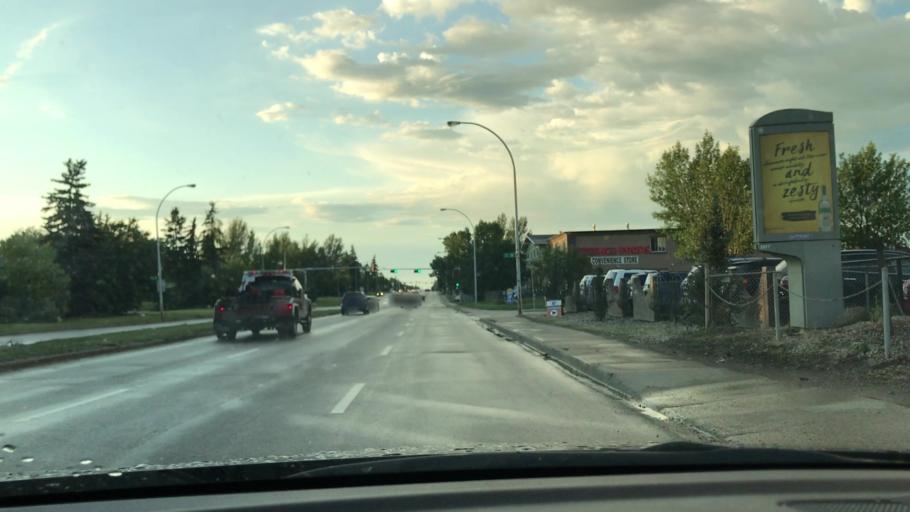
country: CA
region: Alberta
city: Edmonton
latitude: 53.5128
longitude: -113.4428
